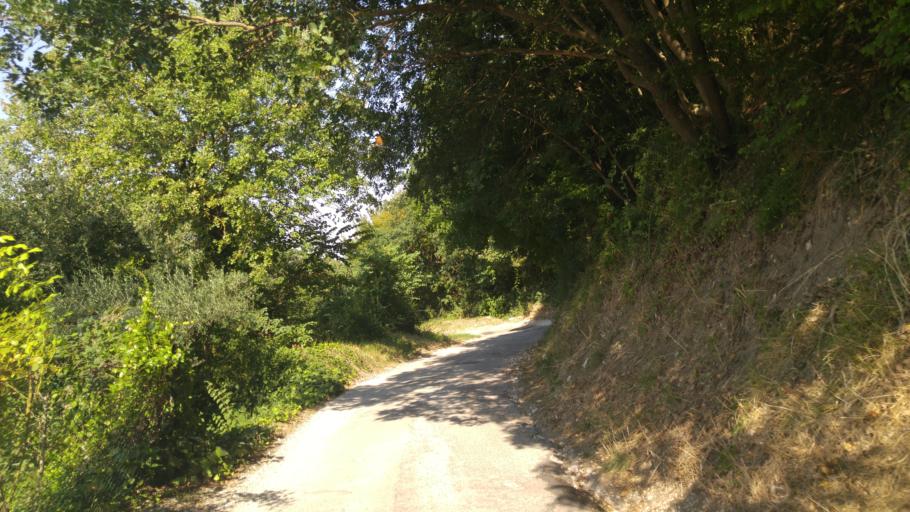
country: IT
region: The Marches
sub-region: Provincia di Pesaro e Urbino
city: Fossombrone
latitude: 43.6808
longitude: 12.8028
